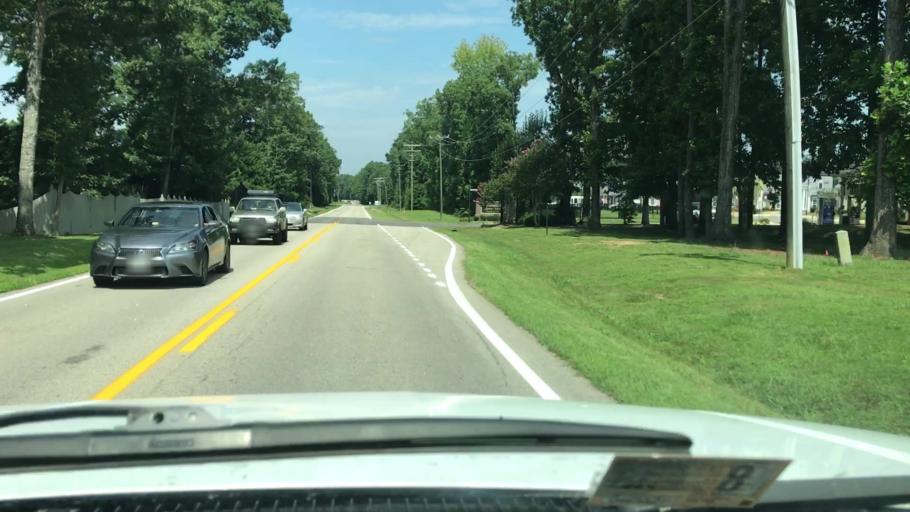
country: US
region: Virginia
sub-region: Chesterfield County
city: Brandermill
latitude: 37.5244
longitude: -77.6656
